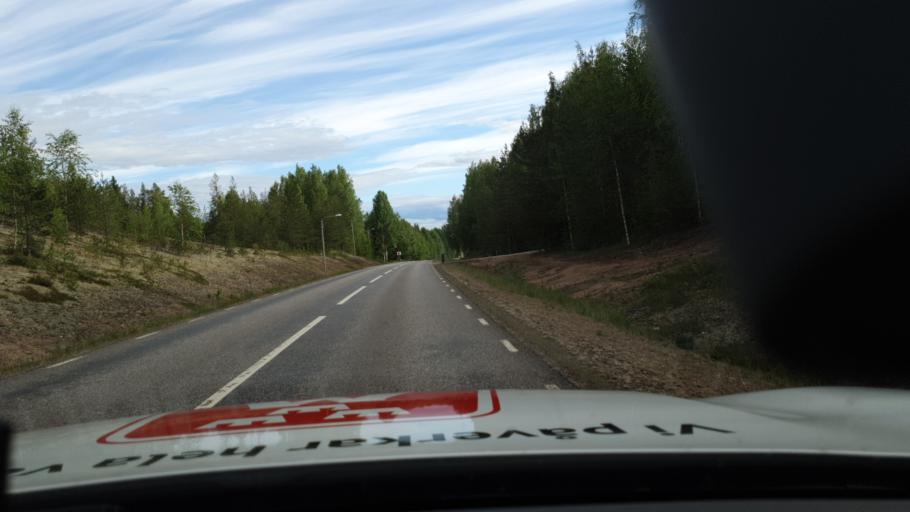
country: SE
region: Norrbotten
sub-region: Overkalix Kommun
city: OEverkalix
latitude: 66.5177
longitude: 22.7656
